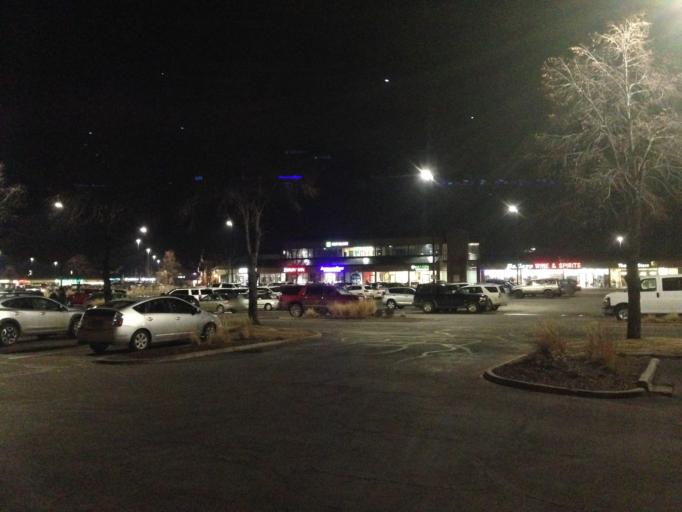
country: US
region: Colorado
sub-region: Boulder County
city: Boulder
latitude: 39.9995
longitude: -105.2356
